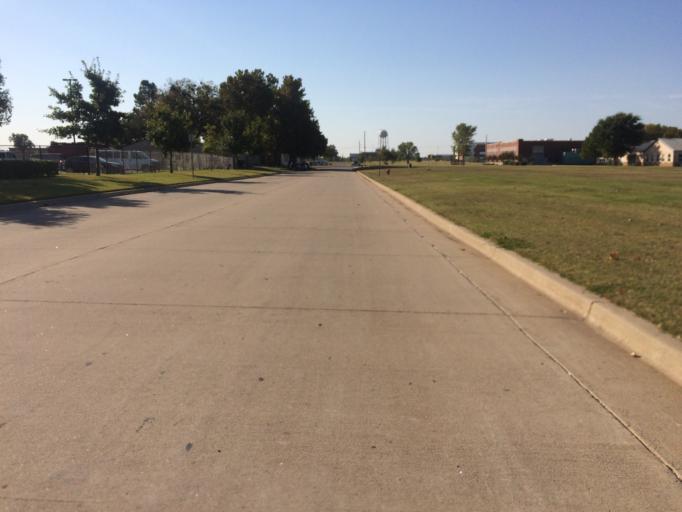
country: US
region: Oklahoma
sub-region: Cleveland County
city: Norman
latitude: 35.1889
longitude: -97.4356
